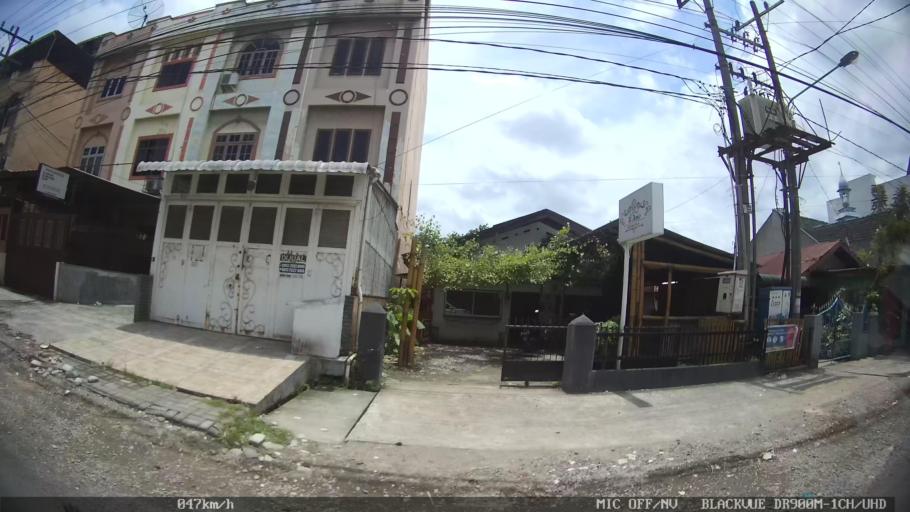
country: ID
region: North Sumatra
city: Medan
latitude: 3.6166
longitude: 98.6851
